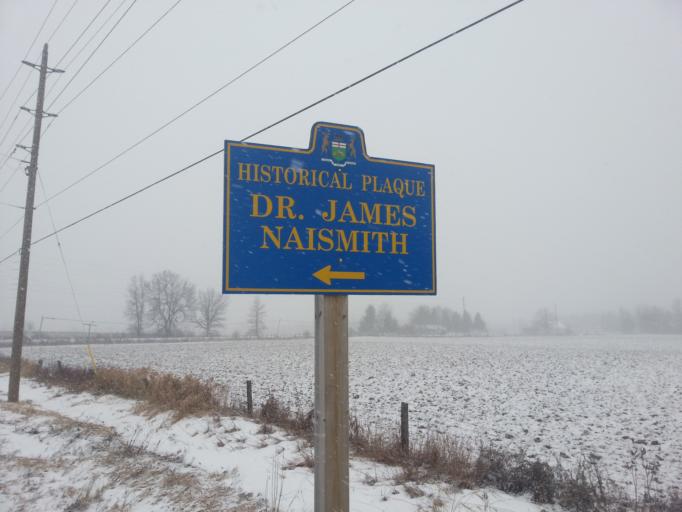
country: CA
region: Ontario
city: Carleton Place
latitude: 45.2418
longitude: -76.2323
